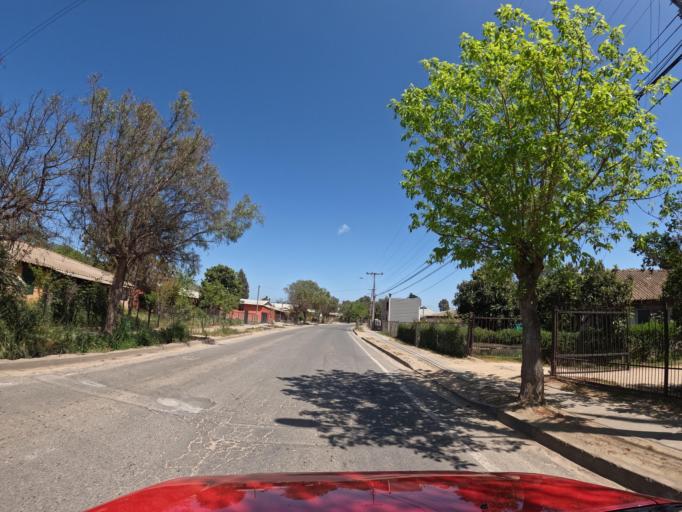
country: CL
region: O'Higgins
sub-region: Provincia de Colchagua
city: Santa Cruz
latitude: -34.7278
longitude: -71.6623
